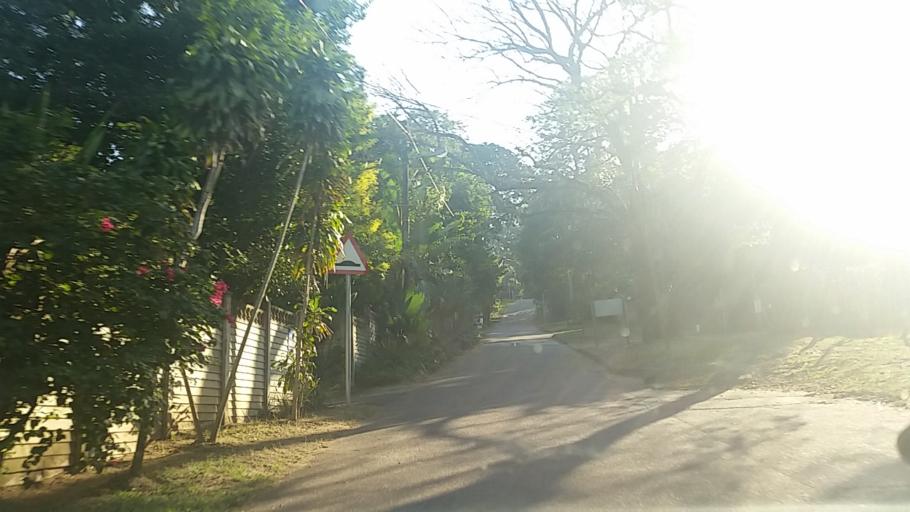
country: ZA
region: KwaZulu-Natal
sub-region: eThekwini Metropolitan Municipality
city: Berea
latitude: -29.8321
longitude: 30.8917
